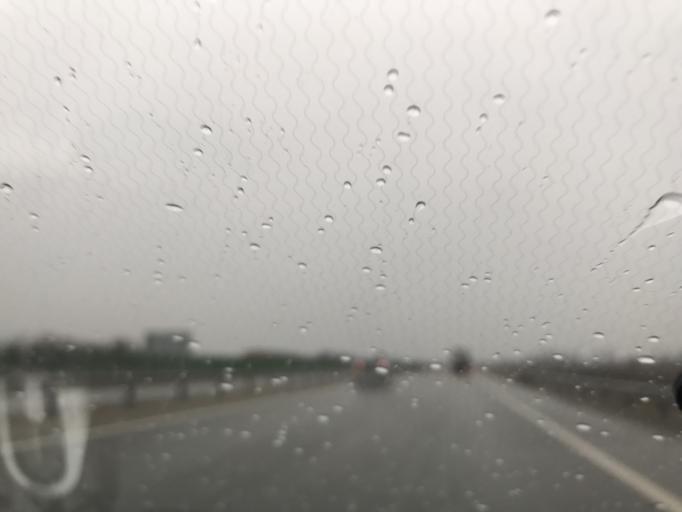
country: RU
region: Krasnodarskiy
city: Krylovskaya
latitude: 46.2917
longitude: 39.8225
